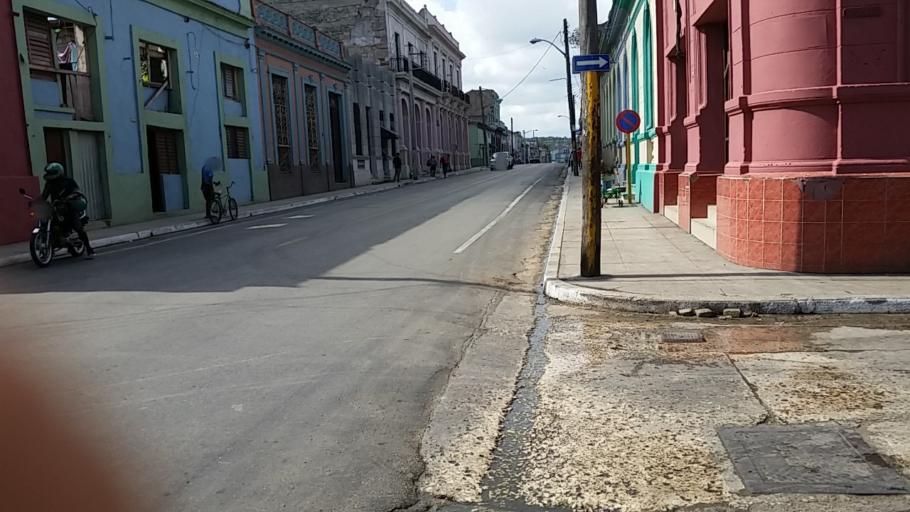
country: CU
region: Matanzas
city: Matanzas
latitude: 23.0402
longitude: -81.5742
